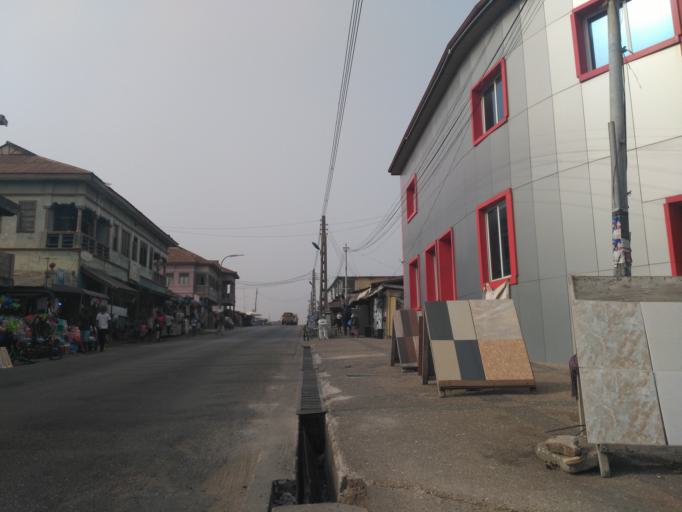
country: GH
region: Ashanti
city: Kumasi
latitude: 6.6853
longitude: -1.6113
